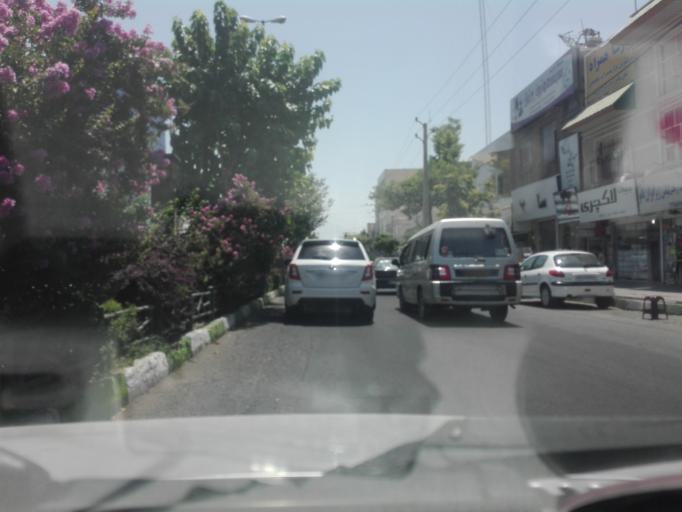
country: IR
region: Tehran
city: Shahre Jadide Andisheh
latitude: 35.7218
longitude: 50.9876
